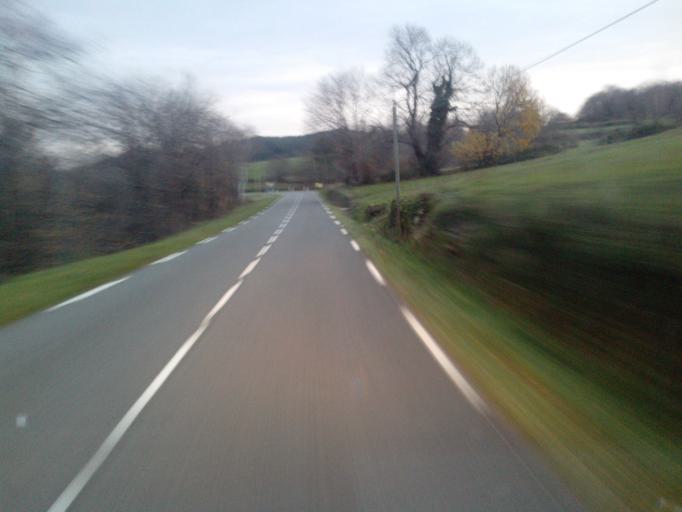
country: FR
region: Languedoc-Roussillon
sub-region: Departement du Gard
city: Saint-Jean-du-Gard
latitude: 44.1506
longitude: 3.7657
